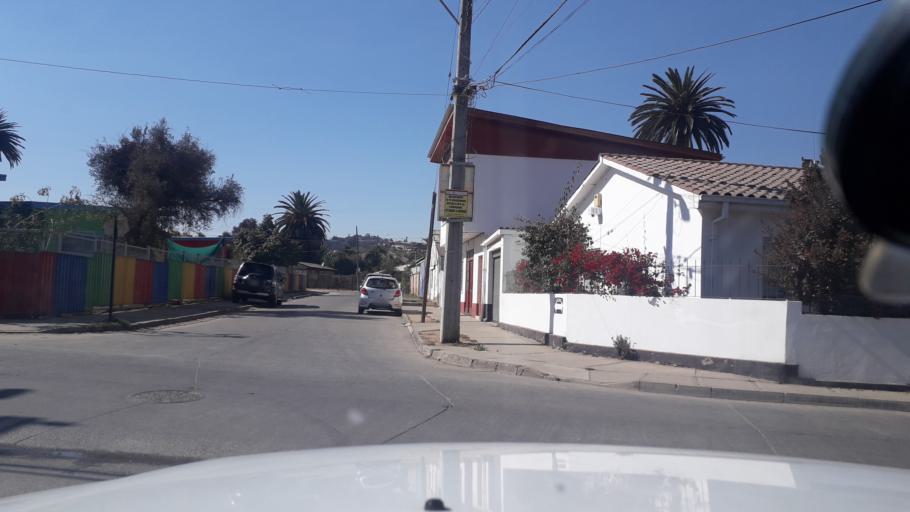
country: CL
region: Valparaiso
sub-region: Provincia de Marga Marga
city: Villa Alemana
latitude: -33.0398
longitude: -71.3539
